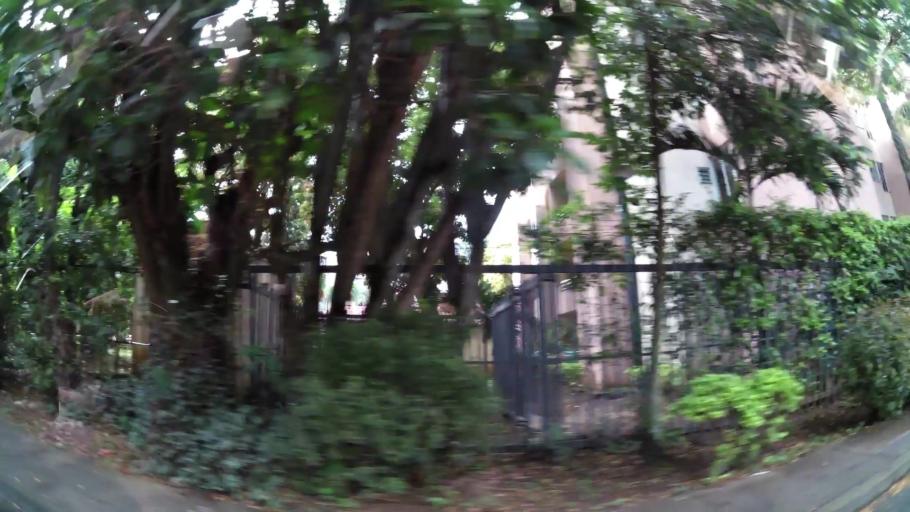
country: CO
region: Valle del Cauca
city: Cali
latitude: 3.3871
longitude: -76.5465
